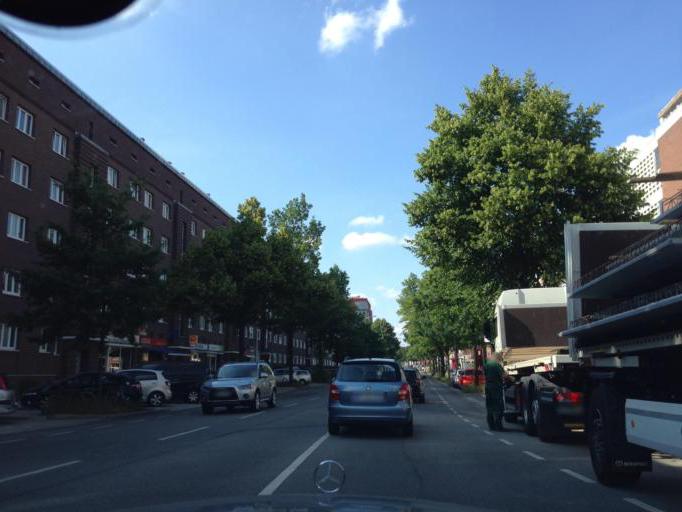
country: DE
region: Hamburg
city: Barmbek-Nord
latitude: 53.5996
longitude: 10.0412
